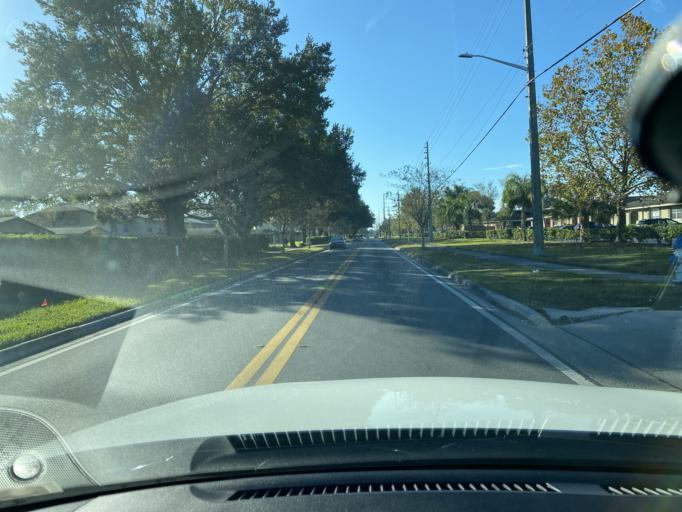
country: US
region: Florida
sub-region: Orange County
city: Azalea Park
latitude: 28.5232
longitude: -81.3021
